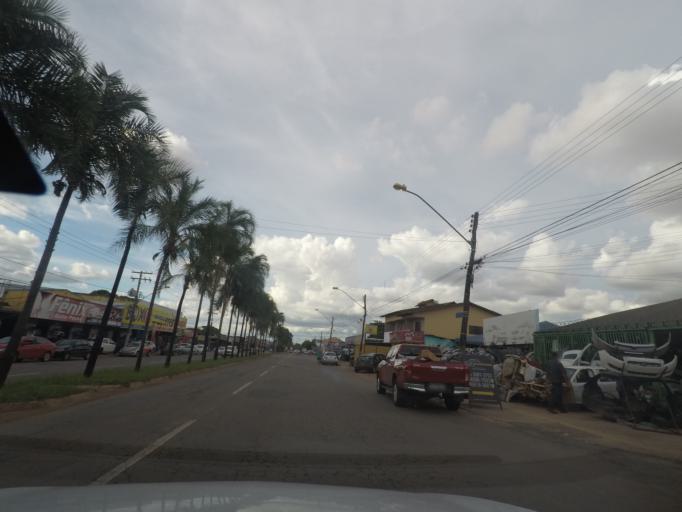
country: BR
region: Goias
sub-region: Goiania
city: Goiania
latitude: -16.7003
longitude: -49.3150
